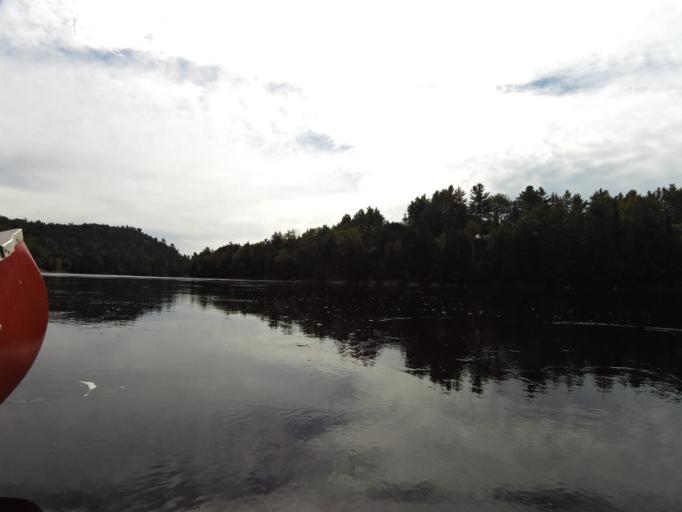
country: CA
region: Quebec
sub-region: Outaouais
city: Wakefield
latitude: 45.7727
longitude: -75.9398
